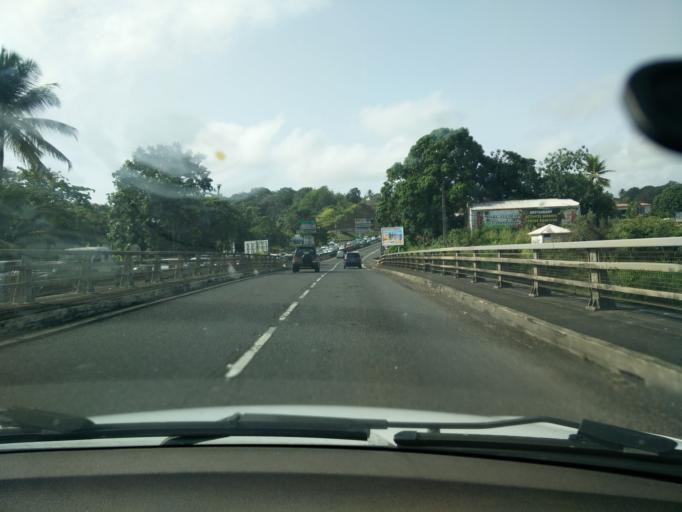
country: GP
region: Guadeloupe
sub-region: Guadeloupe
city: Petit-Bourg
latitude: 16.1998
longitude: -61.6061
